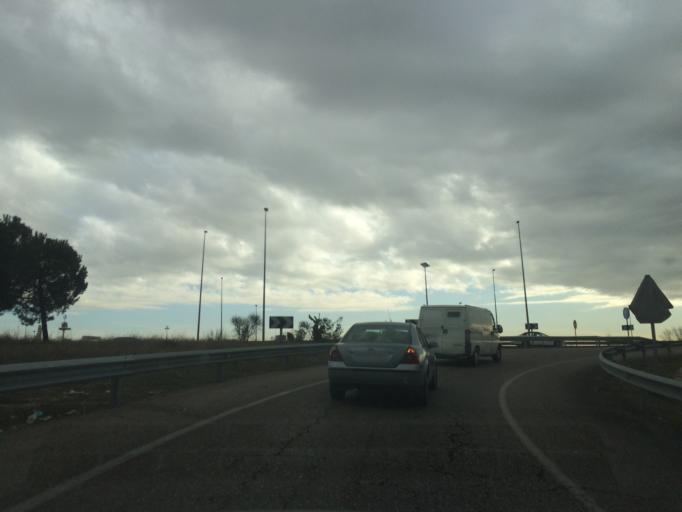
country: ES
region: Madrid
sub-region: Provincia de Madrid
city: Mostoles
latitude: 40.3480
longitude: -3.8572
